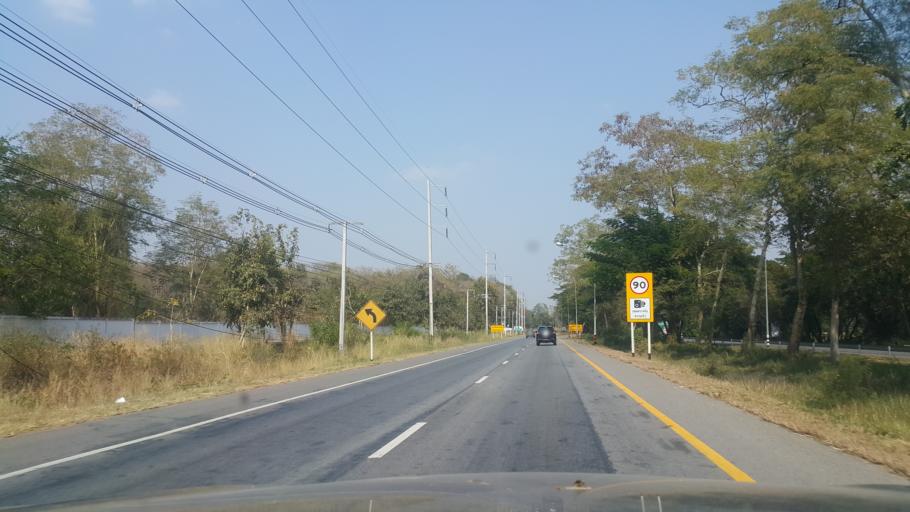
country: TH
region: Nakhon Ratchasima
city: Pak Thong Chai
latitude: 14.5991
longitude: 102.0055
